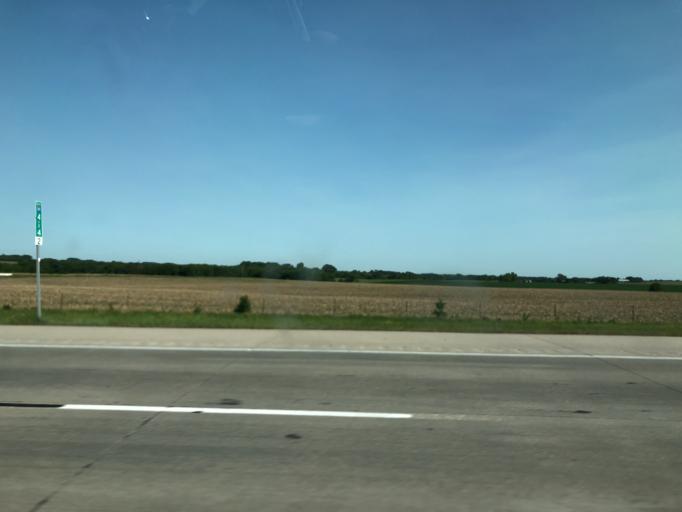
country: US
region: Nebraska
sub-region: Lancaster County
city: Waverly
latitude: 40.9107
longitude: -96.4869
